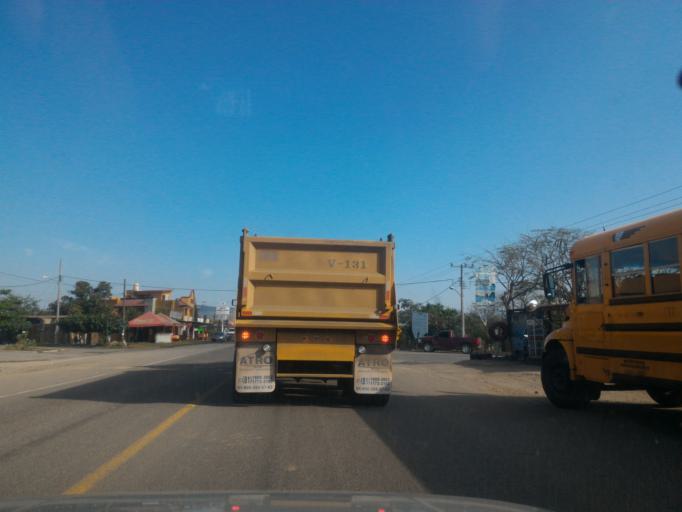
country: MX
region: Michoacan
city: Coahuayana Viejo
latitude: 18.7524
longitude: -103.7243
